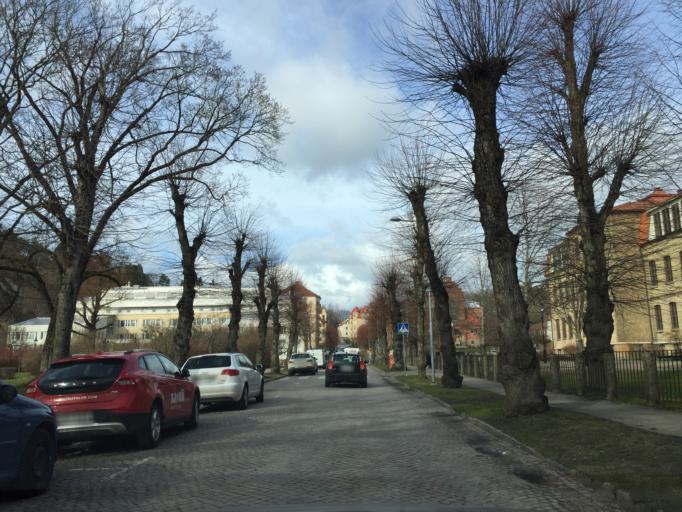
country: SE
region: Vaestra Goetaland
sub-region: Uddevalla Kommun
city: Uddevalla
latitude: 58.3500
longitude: 11.9407
